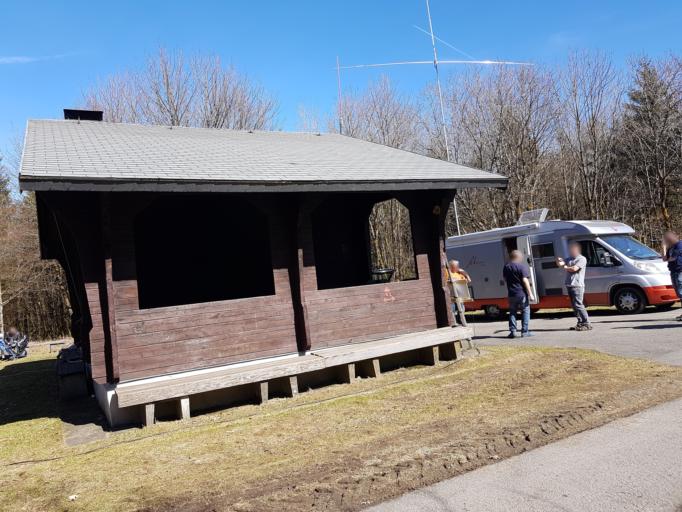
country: DE
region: North Rhine-Westphalia
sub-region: Regierungsbezirk Arnsberg
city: Bad Fredeburg
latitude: 51.2034
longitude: 8.3679
